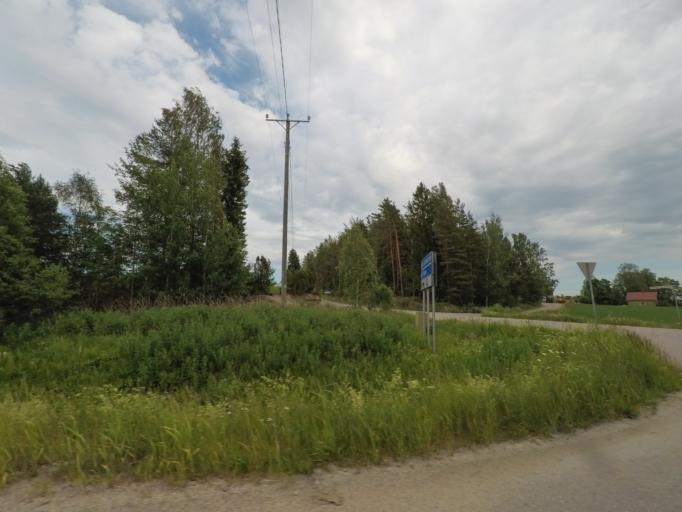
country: FI
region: Uusimaa
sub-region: Porvoo
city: Pukkila
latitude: 60.8048
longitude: 25.4777
